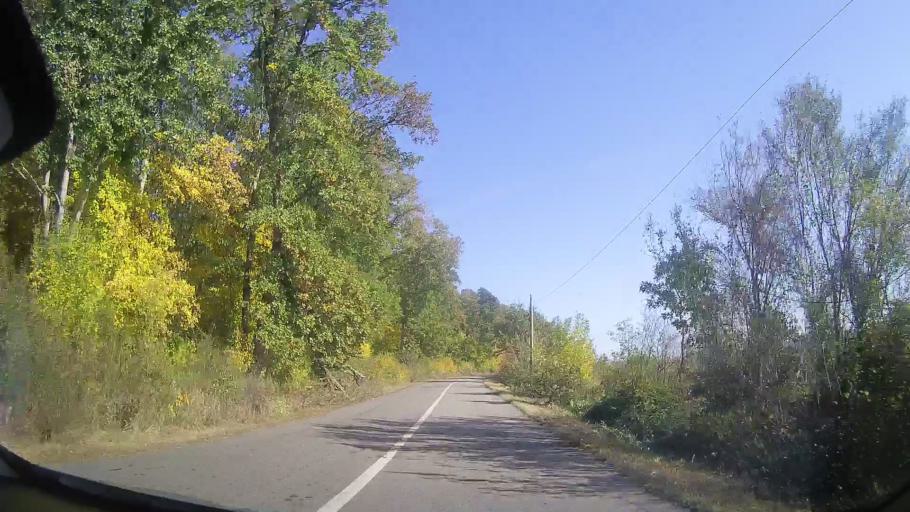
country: RO
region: Timis
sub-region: Comuna Ghizela
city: Ghizela
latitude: 45.8369
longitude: 21.7761
